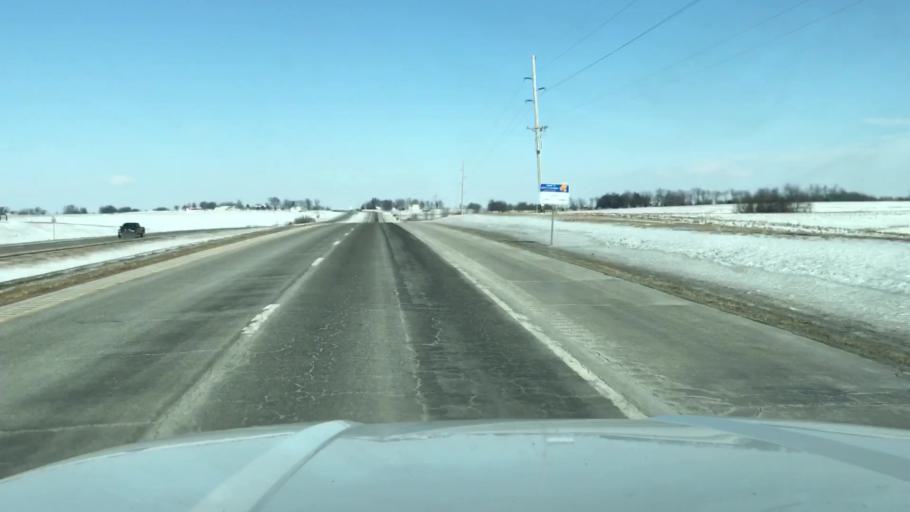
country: US
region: Missouri
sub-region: Nodaway County
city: Maryville
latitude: 40.2595
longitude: -94.8668
